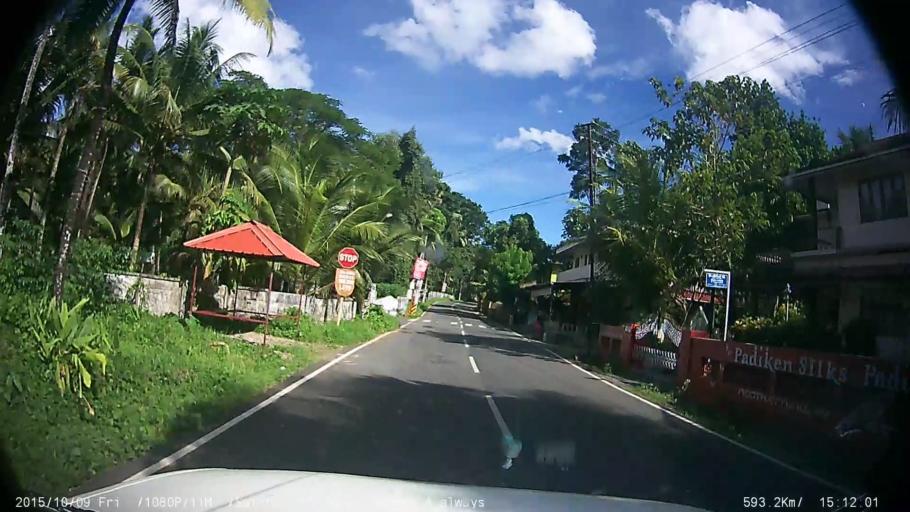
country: IN
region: Kerala
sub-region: Ernakulam
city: Piravam
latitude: 9.8732
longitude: 76.5825
